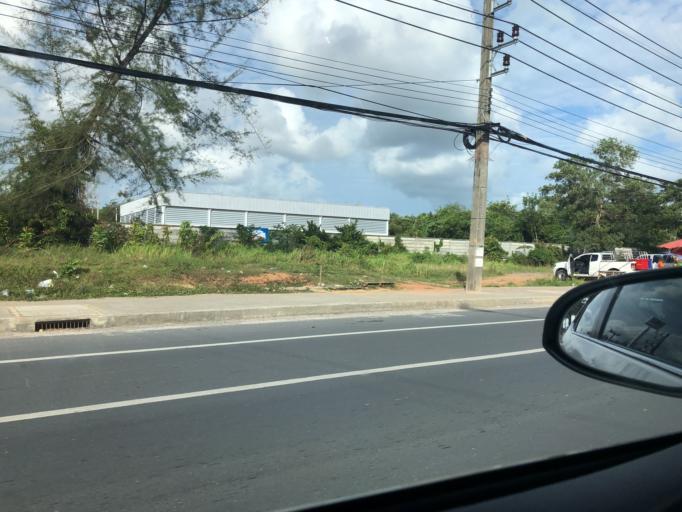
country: TH
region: Phuket
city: Thalang
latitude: 8.0191
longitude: 98.3368
